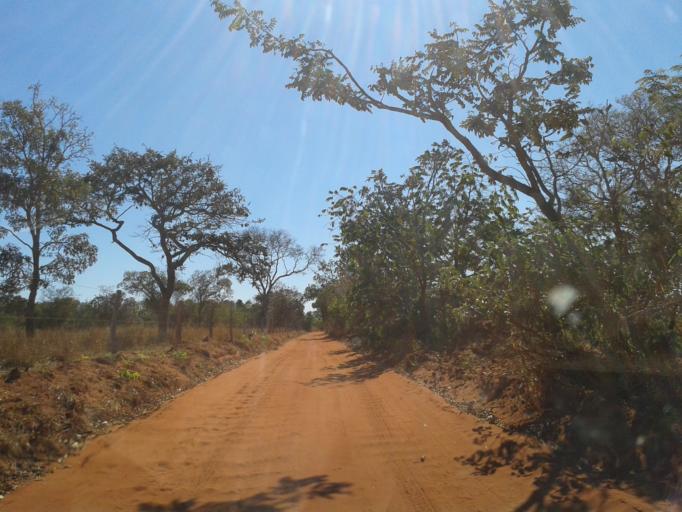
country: BR
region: Minas Gerais
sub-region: Ituiutaba
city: Ituiutaba
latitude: -19.0730
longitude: -49.3358
